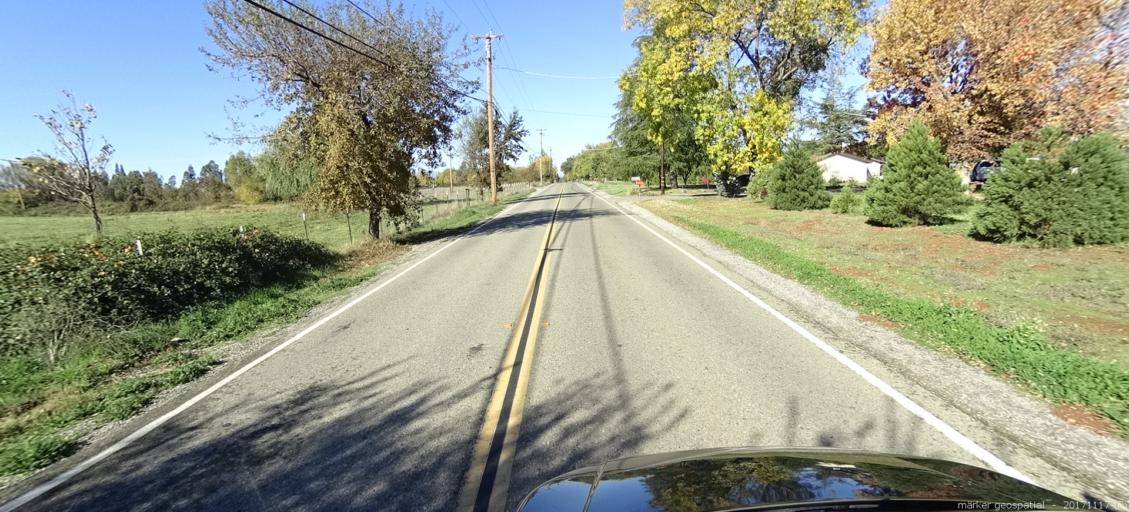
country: US
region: California
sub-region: Shasta County
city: Cottonwood
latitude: 40.4234
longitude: -122.2212
